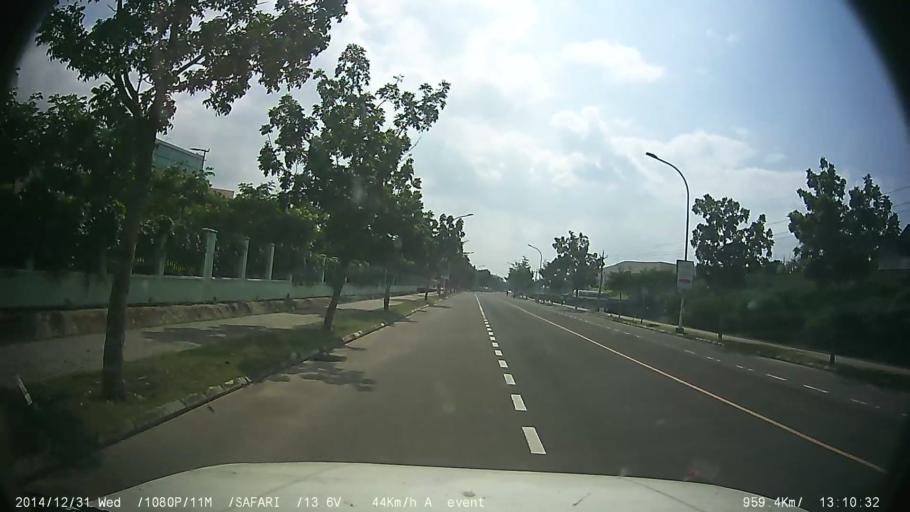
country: IN
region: Tamil Nadu
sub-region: Kancheepuram
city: Singapperumalkovil
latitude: 12.7366
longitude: 80.0027
